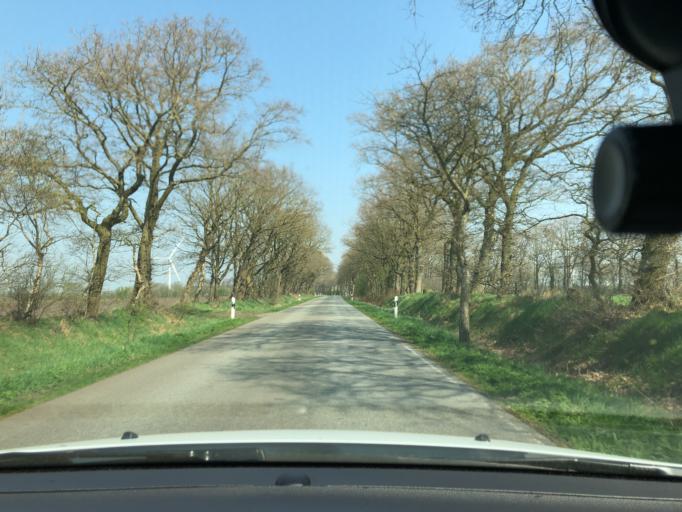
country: DE
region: Schleswig-Holstein
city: Goldebek
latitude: 54.6830
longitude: 9.1558
